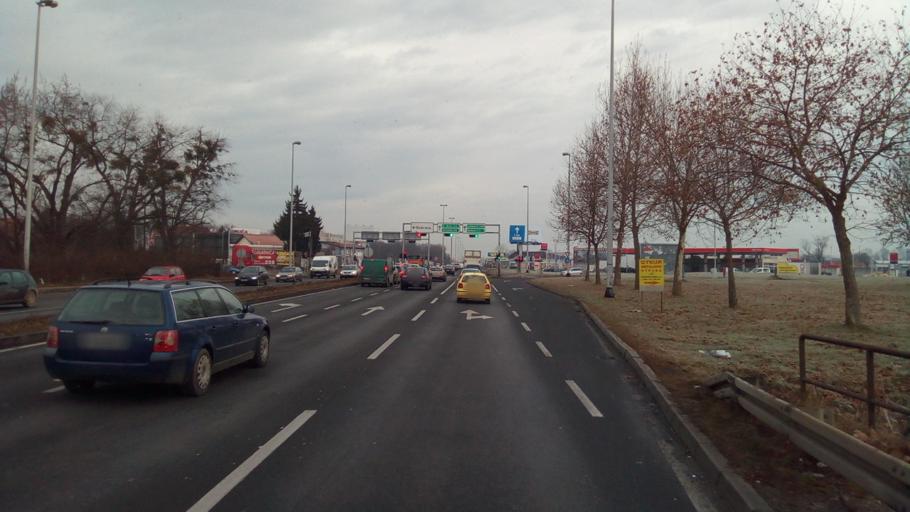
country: HR
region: Grad Zagreb
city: Dubrava
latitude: 45.8030
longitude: 16.0743
